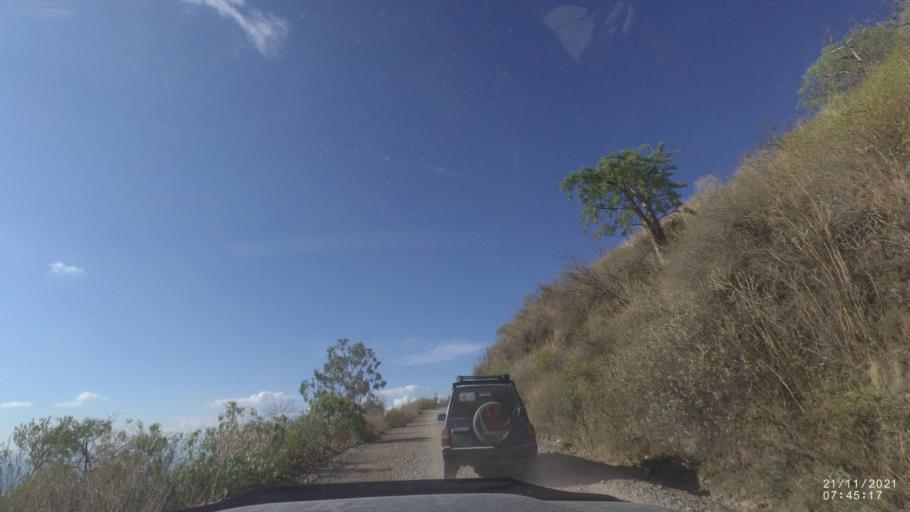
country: BO
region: Cochabamba
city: Cochabamba
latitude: -17.3148
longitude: -66.2190
